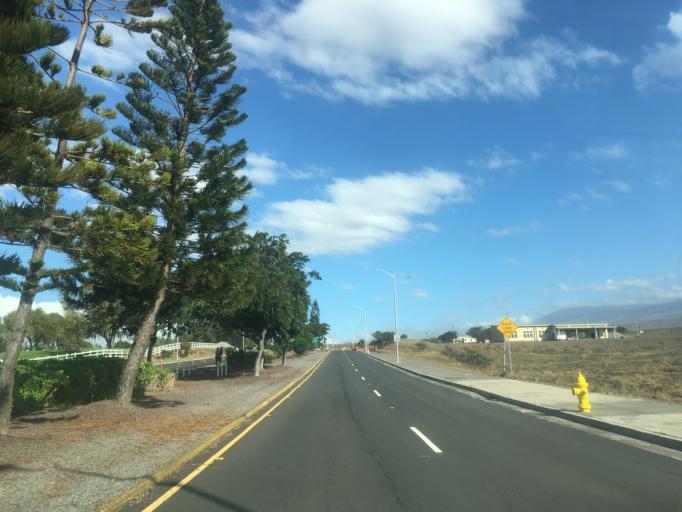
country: US
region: Hawaii
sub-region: Hawaii County
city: Waikoloa
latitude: 19.9258
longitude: -155.7918
